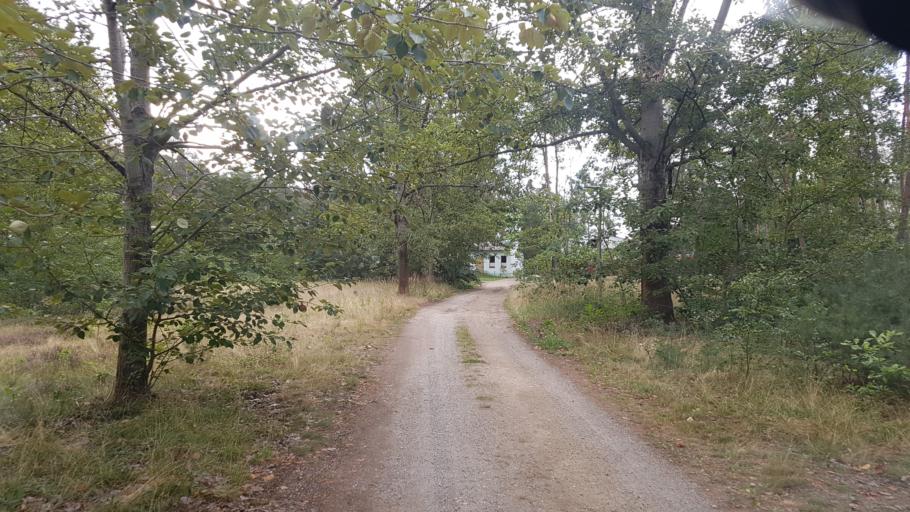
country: DE
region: Brandenburg
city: Ruckersdorf
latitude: 51.5748
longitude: 13.5787
